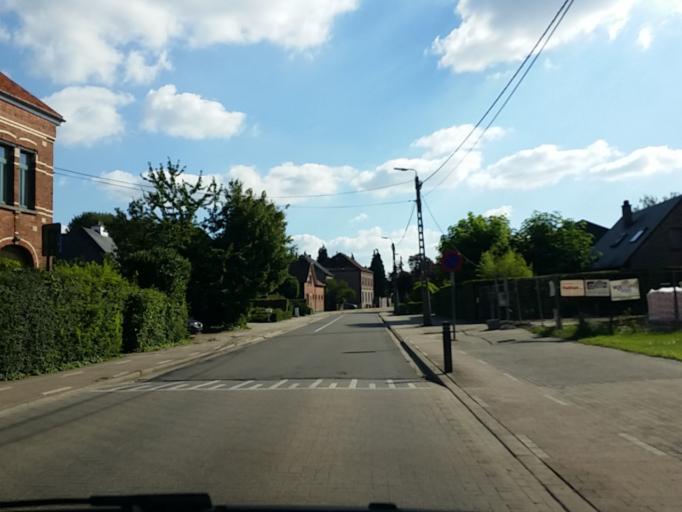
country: BE
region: Flanders
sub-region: Provincie Vlaams-Brabant
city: Rotselaar
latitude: 50.9359
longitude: 4.6970
